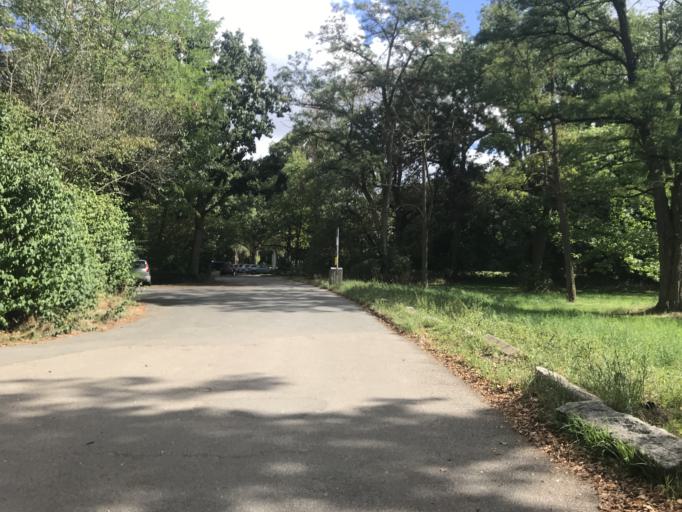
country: DE
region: Rheinland-Pfalz
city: Mainz
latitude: 50.0001
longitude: 8.2902
